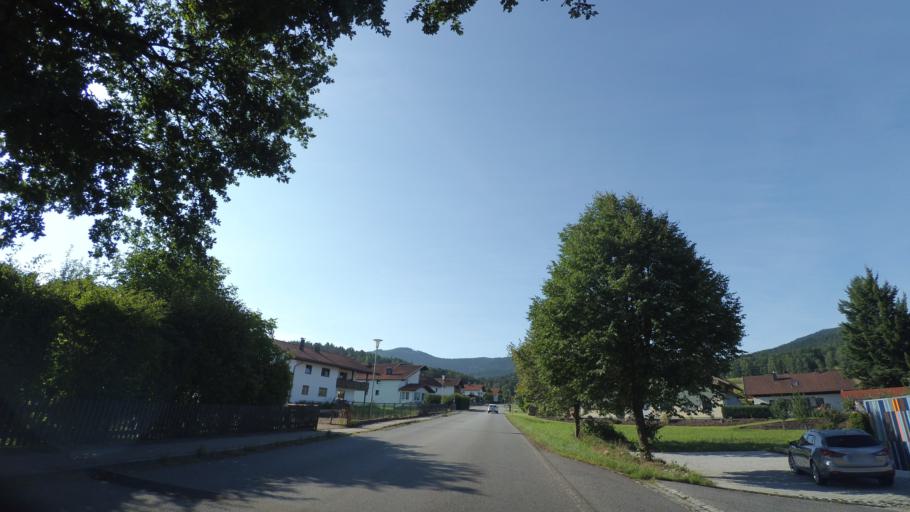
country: DE
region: Bavaria
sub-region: Upper Palatinate
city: Arrach
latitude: 49.1946
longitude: 13.0025
